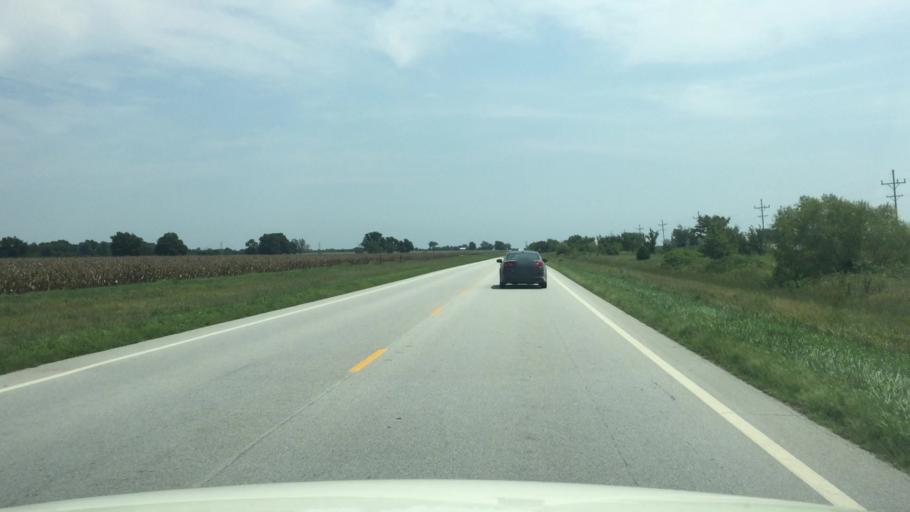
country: US
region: Kansas
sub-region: Cherokee County
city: Columbus
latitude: 37.1792
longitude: -94.9288
